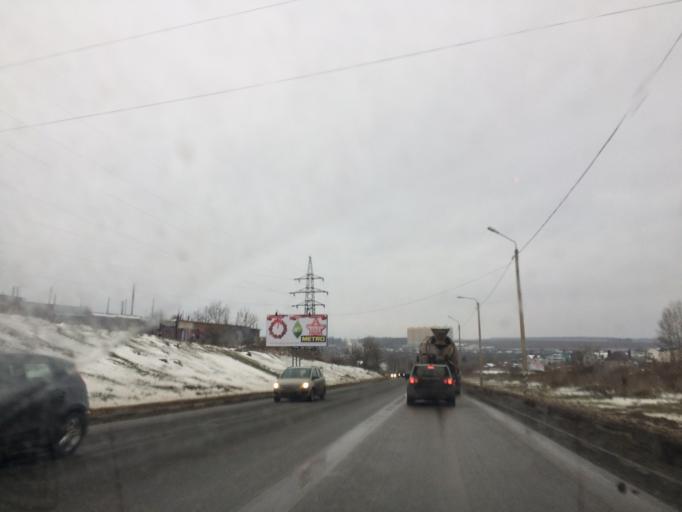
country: RU
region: Tula
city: Mendeleyevskiy
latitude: 54.1574
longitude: 37.5728
